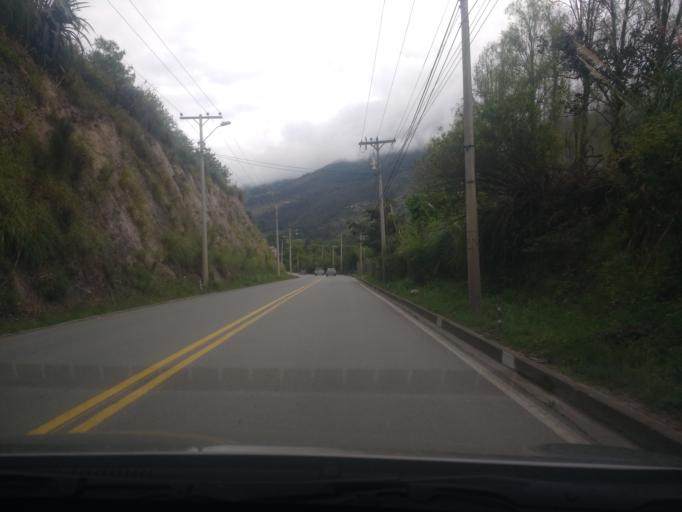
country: EC
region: Azuay
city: La Union
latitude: -2.8472
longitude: -78.7750
